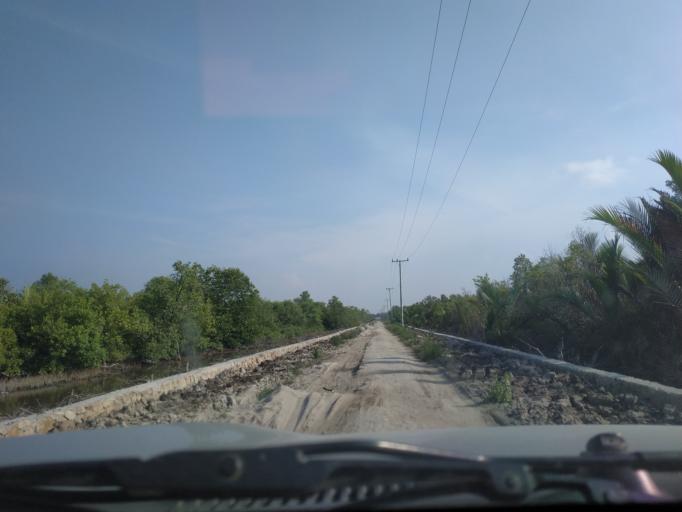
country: ID
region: North Sumatra
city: Teluk Nibung
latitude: 3.1048
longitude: 99.7777
